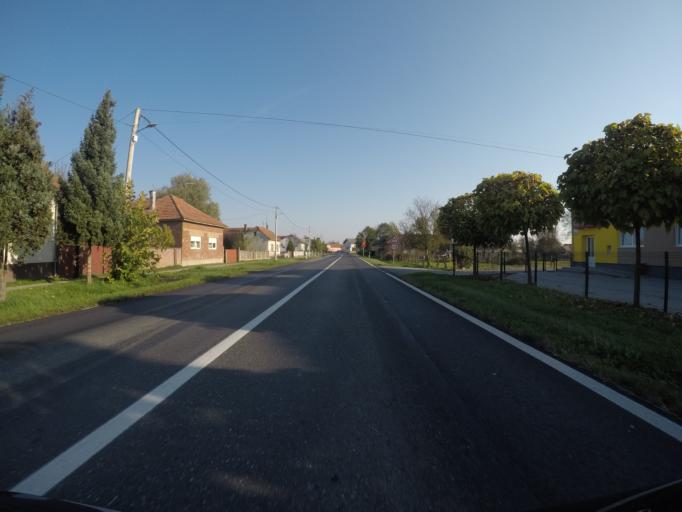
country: HR
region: Koprivnicko-Krizevacka
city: Kalinovac
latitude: 45.9855
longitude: 17.1396
